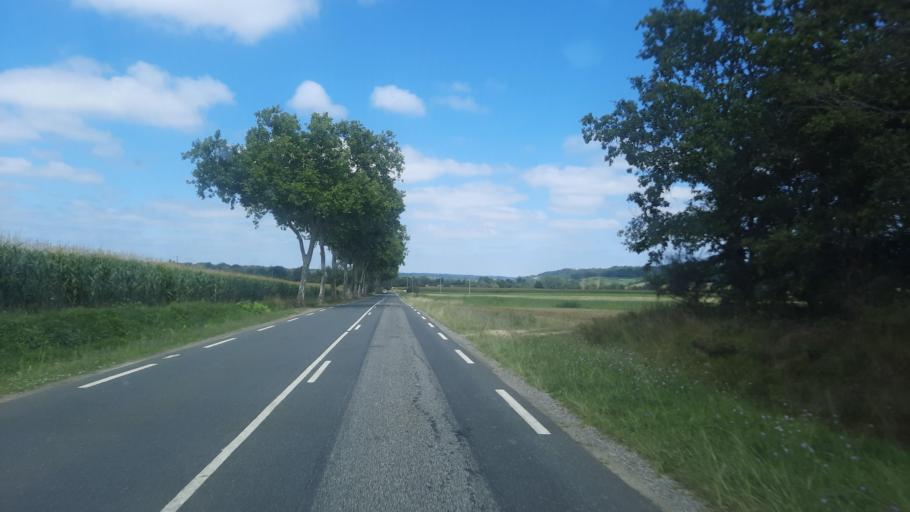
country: FR
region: Midi-Pyrenees
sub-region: Departement de la Haute-Garonne
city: Boulogne-sur-Gesse
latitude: 43.3065
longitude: 0.6767
